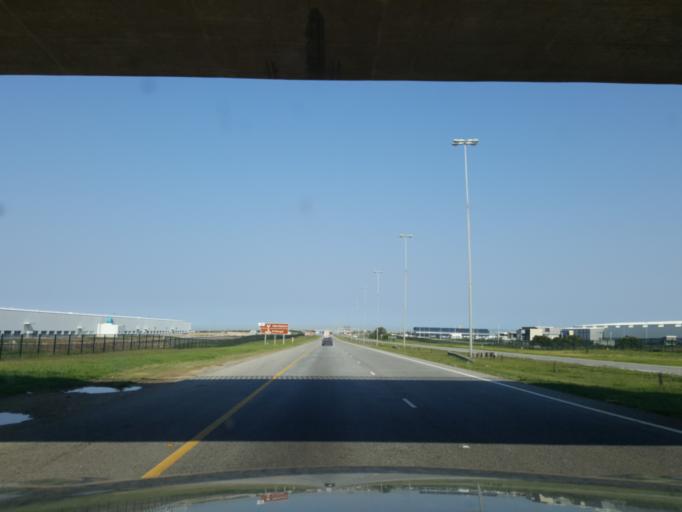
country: ZA
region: Eastern Cape
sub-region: Nelson Mandela Bay Metropolitan Municipality
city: Port Elizabeth
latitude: -33.8124
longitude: 25.6514
